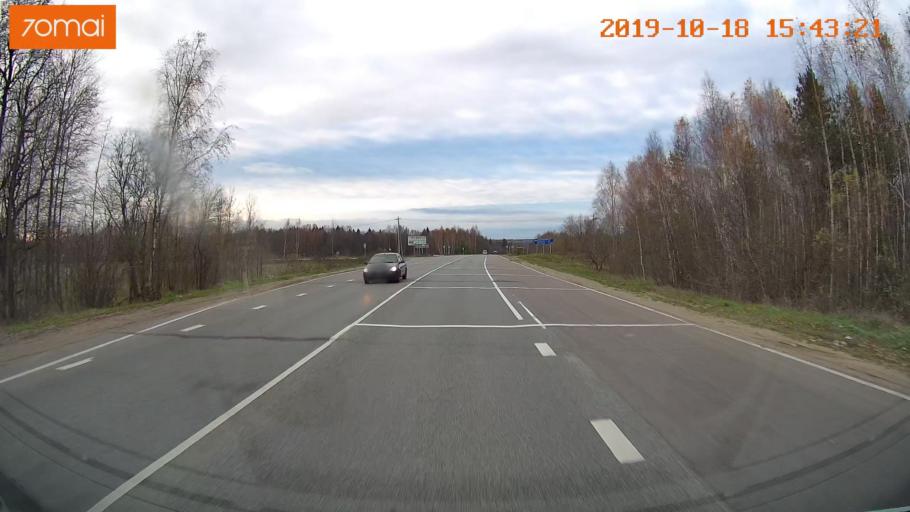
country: RU
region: Vladimir
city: Golovino
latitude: 55.9661
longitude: 40.5526
